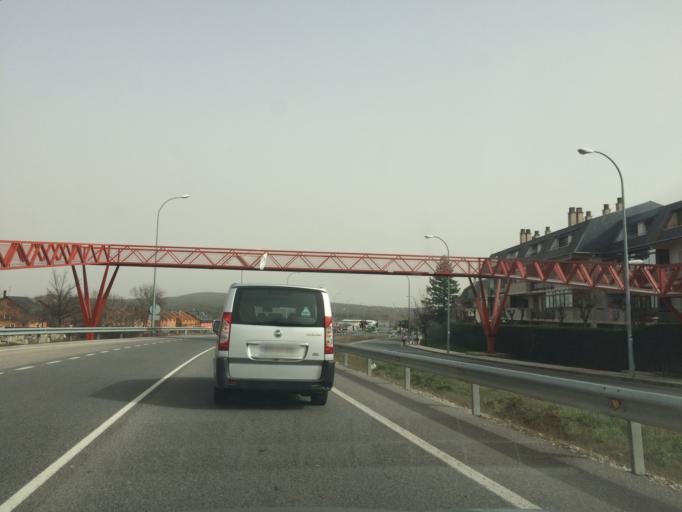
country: ES
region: Madrid
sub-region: Provincia de Madrid
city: Boalo
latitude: 40.6999
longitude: -3.9354
